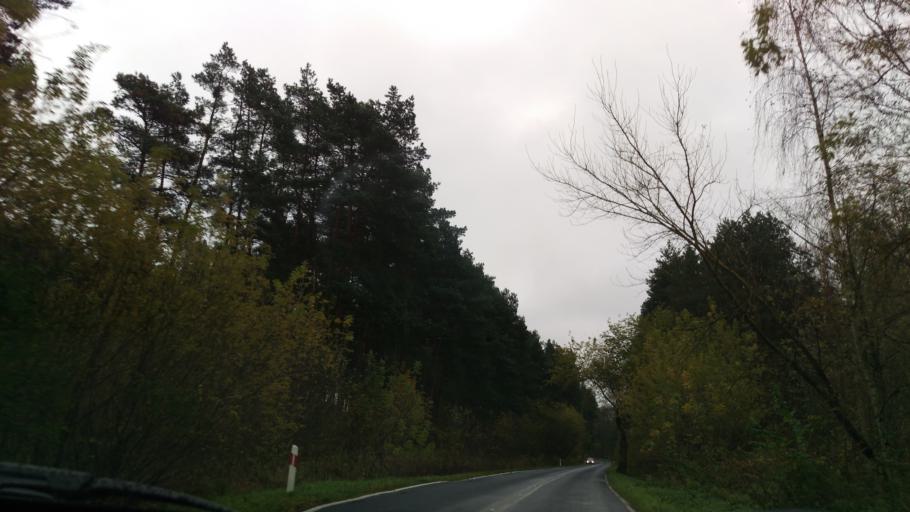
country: PL
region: West Pomeranian Voivodeship
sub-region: Powiat gryfinski
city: Stare Czarnowo
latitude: 53.3940
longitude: 14.7098
